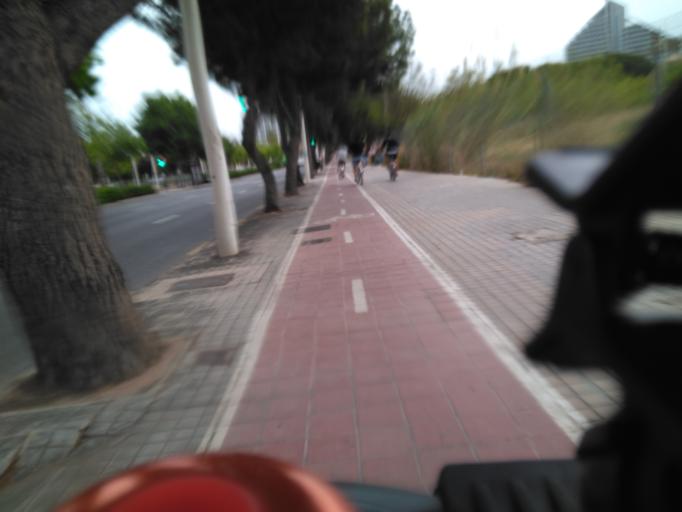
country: ES
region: Valencia
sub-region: Provincia de Valencia
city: Mislata
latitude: 39.4768
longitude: -0.4067
